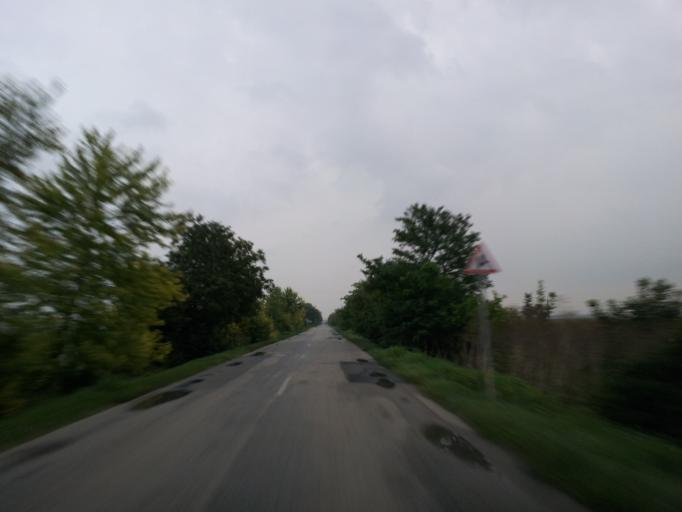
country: HU
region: Tolna
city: Fadd
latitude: 46.4856
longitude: 18.8616
